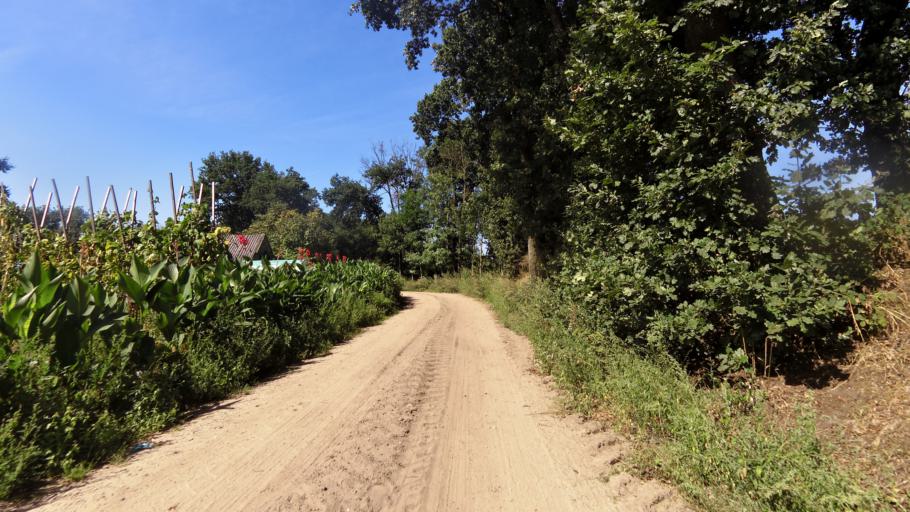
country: NL
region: Gelderland
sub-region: Gemeente Ede
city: Harskamp
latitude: 52.1355
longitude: 5.7614
